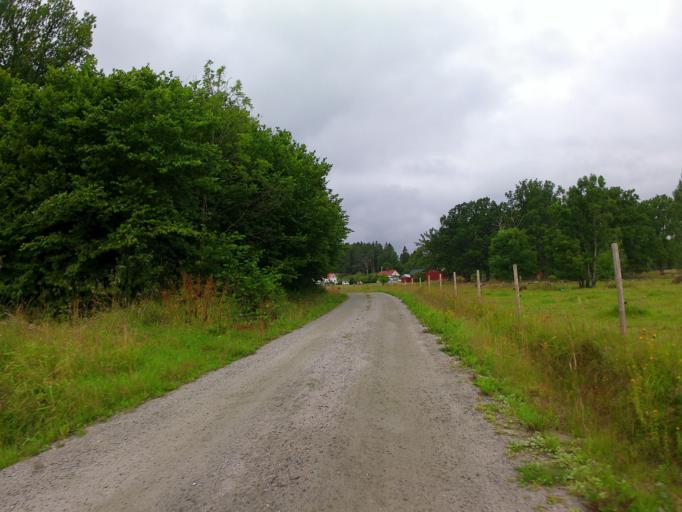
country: SE
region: Vaestra Goetaland
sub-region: Vargarda Kommun
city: Jonstorp
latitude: 58.0319
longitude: 12.6272
